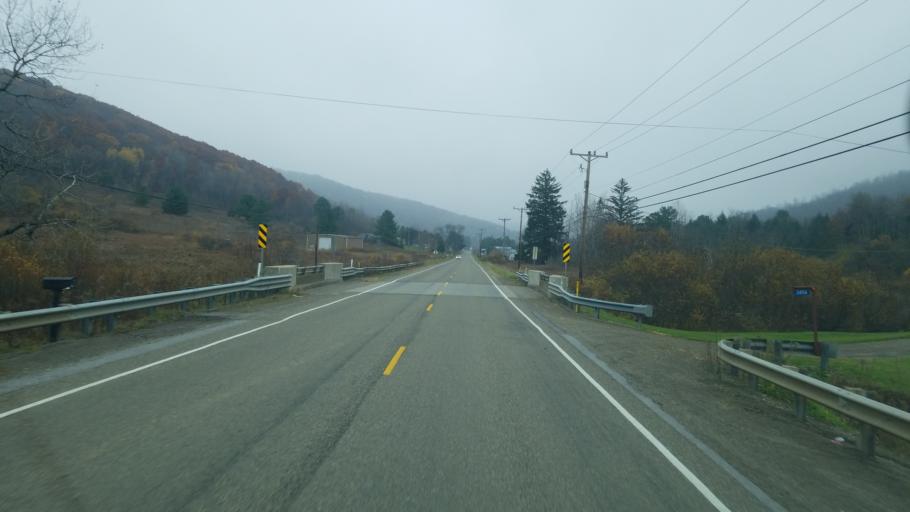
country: US
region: Pennsylvania
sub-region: McKean County
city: Smethport
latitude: 41.8790
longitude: -78.4890
